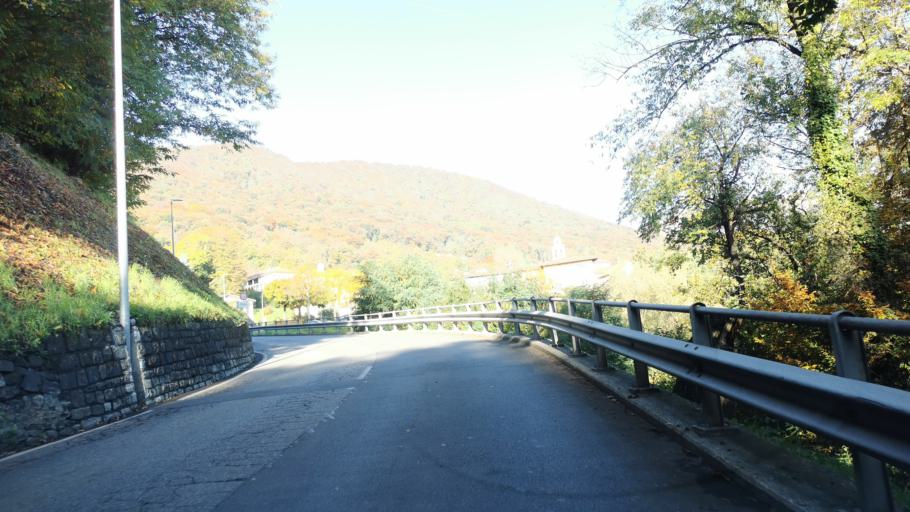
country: CH
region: Ticino
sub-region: Lugano District
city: Pura
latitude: 45.9836
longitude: 8.8718
